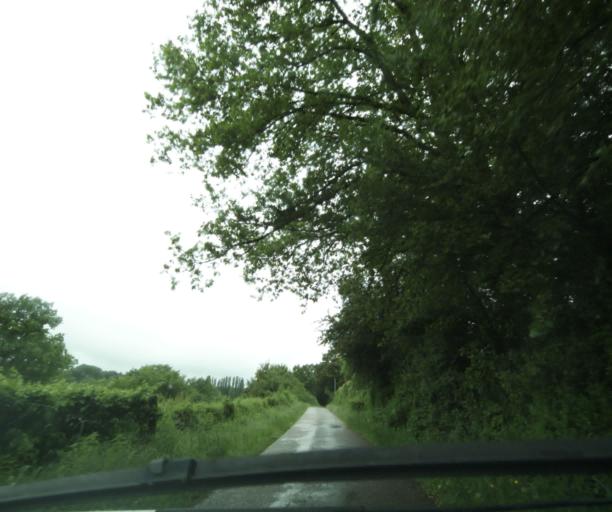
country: FR
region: Bourgogne
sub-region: Departement de Saone-et-Loire
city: Charolles
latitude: 46.4112
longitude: 4.3170
